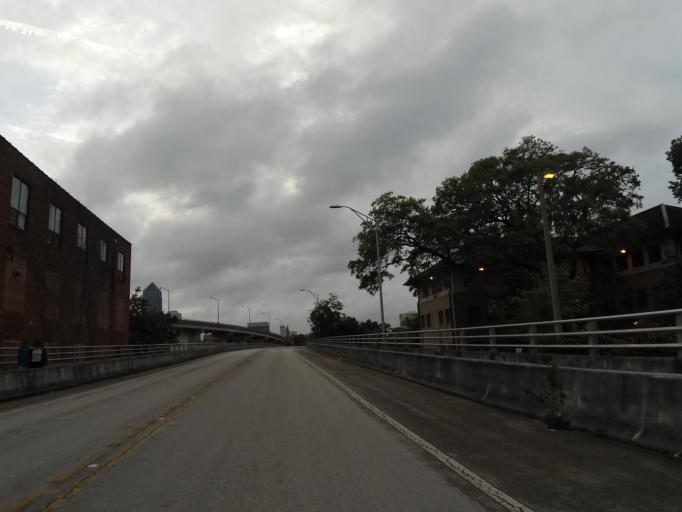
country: US
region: Florida
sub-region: Duval County
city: Jacksonville
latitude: 30.3268
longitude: -81.6468
